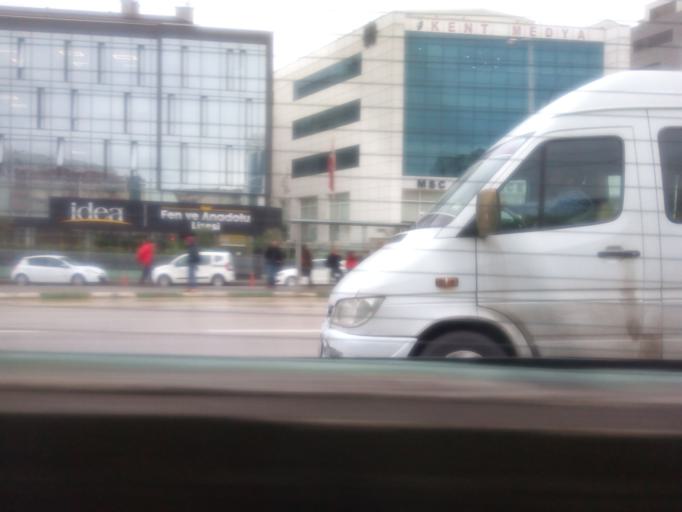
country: TR
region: Bursa
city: Yildirim
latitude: 40.2332
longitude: 28.9807
